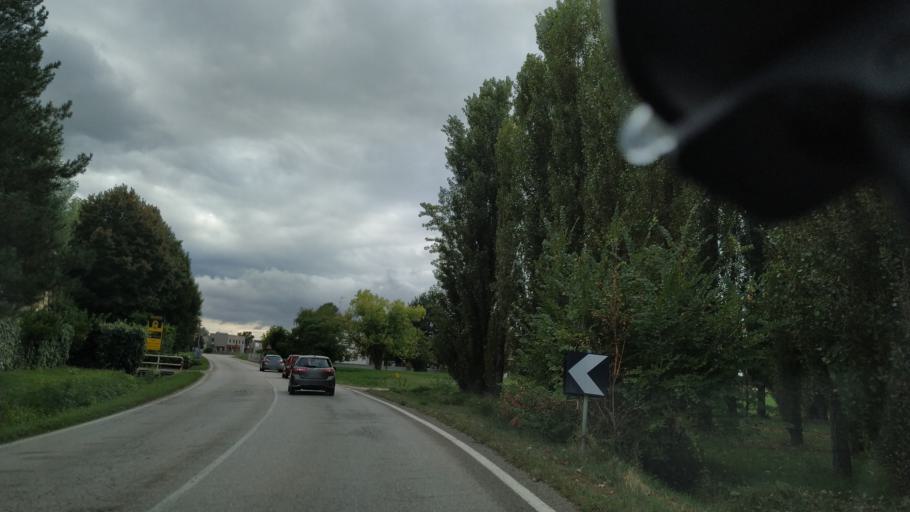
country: IT
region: Emilia-Romagna
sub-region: Provincia di Ferrara
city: Dosso
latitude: 44.7727
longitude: 11.3469
